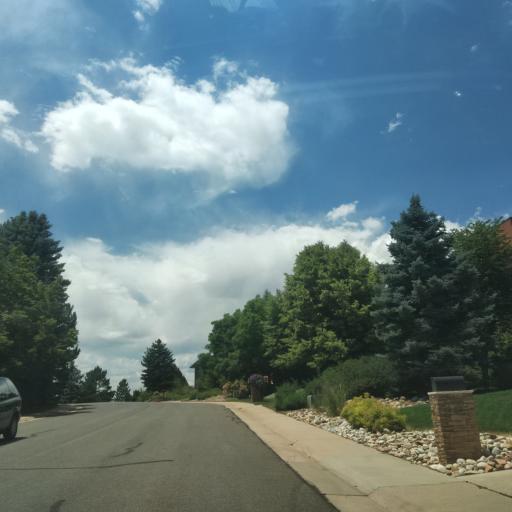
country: US
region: Colorado
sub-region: Jefferson County
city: Lakewood
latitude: 39.6746
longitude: -105.0914
